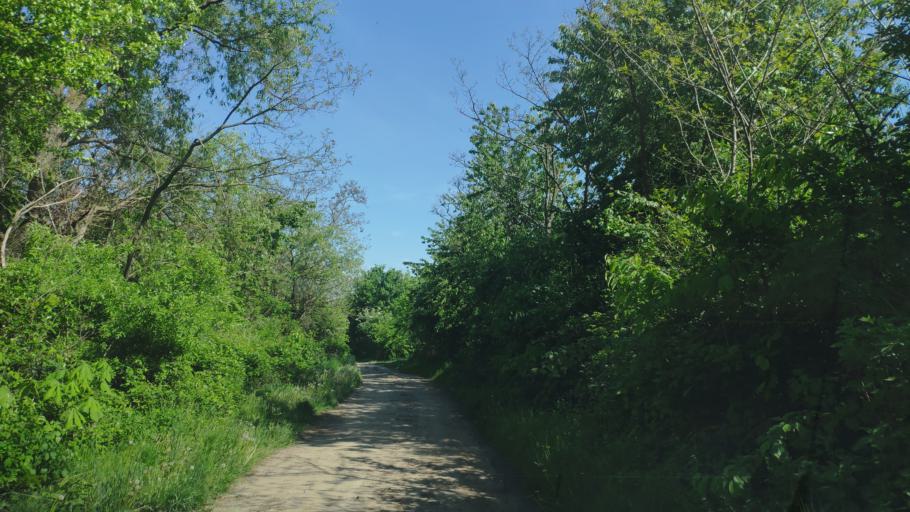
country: SK
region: Kosicky
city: Secovce
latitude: 48.6896
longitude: 21.6011
